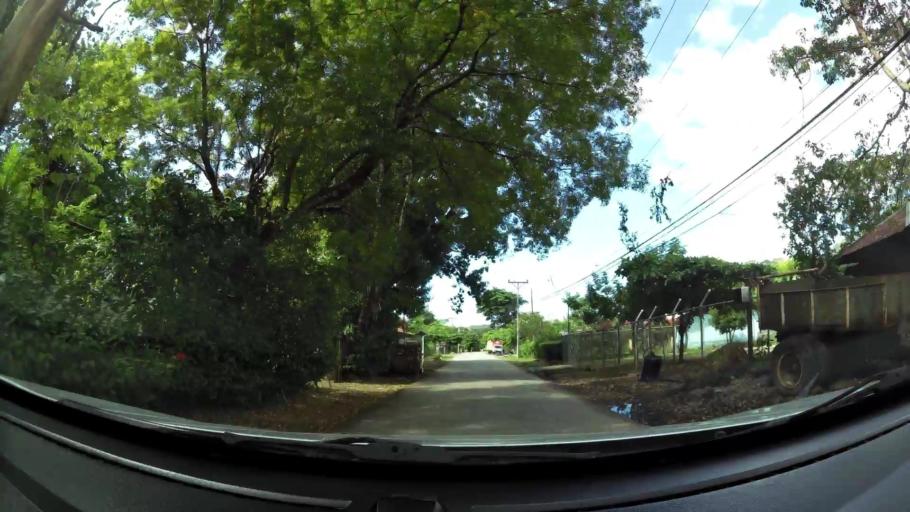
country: CR
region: Guanacaste
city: Juntas
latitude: 10.2811
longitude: -84.9422
